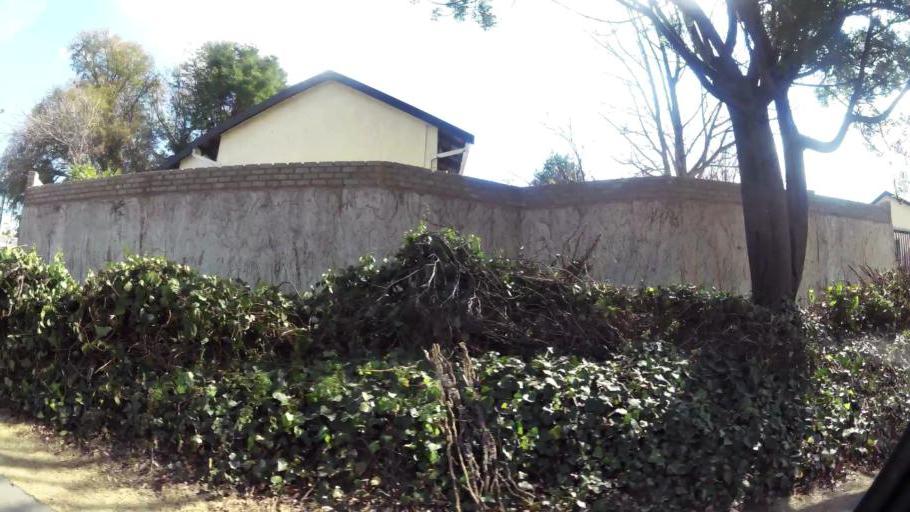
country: ZA
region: Gauteng
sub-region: West Rand District Municipality
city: Muldersdriseloop
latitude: -26.0704
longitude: 27.9454
